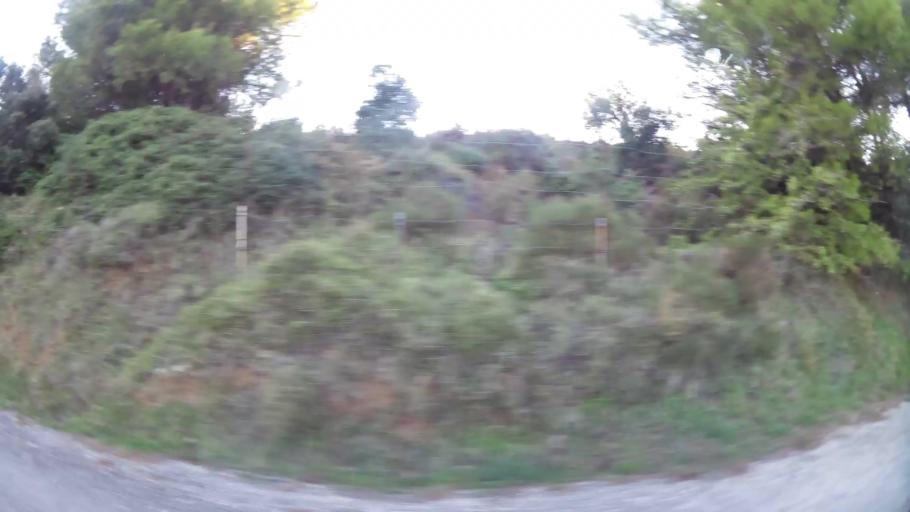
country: GR
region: Attica
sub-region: Nomarchia Anatolikis Attikis
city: Kryoneri
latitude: 38.1476
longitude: 23.8355
